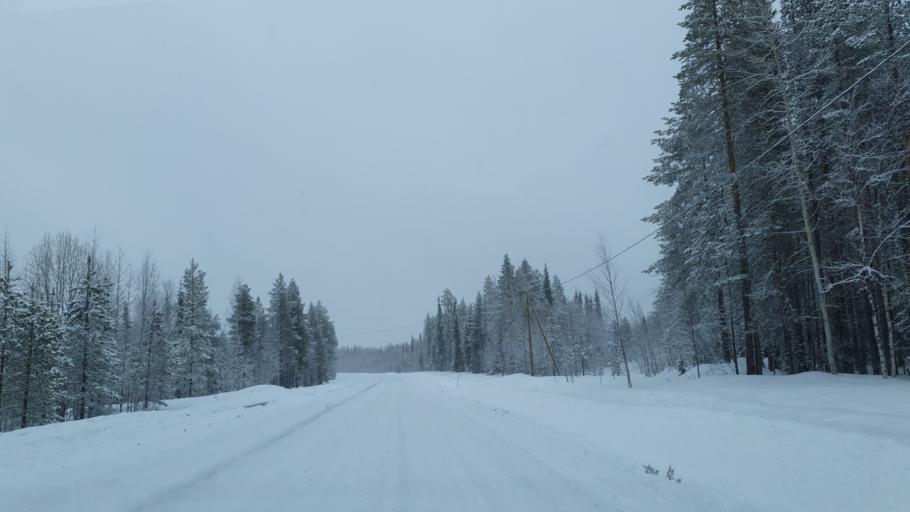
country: FI
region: Lapland
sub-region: Tunturi-Lappi
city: Kittilae
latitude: 67.6613
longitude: 24.8192
